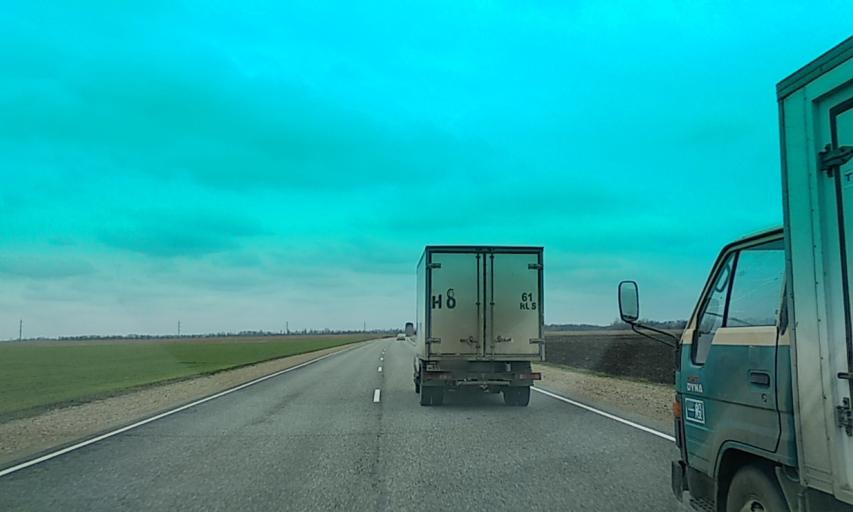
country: RU
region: Adygeya
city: Khatukay
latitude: 45.1525
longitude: 39.6469
